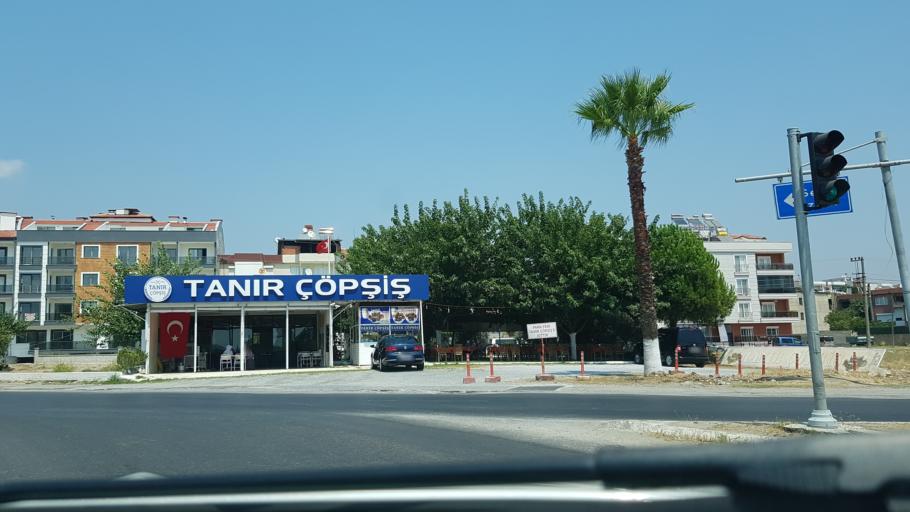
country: TR
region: Aydin
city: Ortaklar
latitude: 37.8836
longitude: 27.5057
